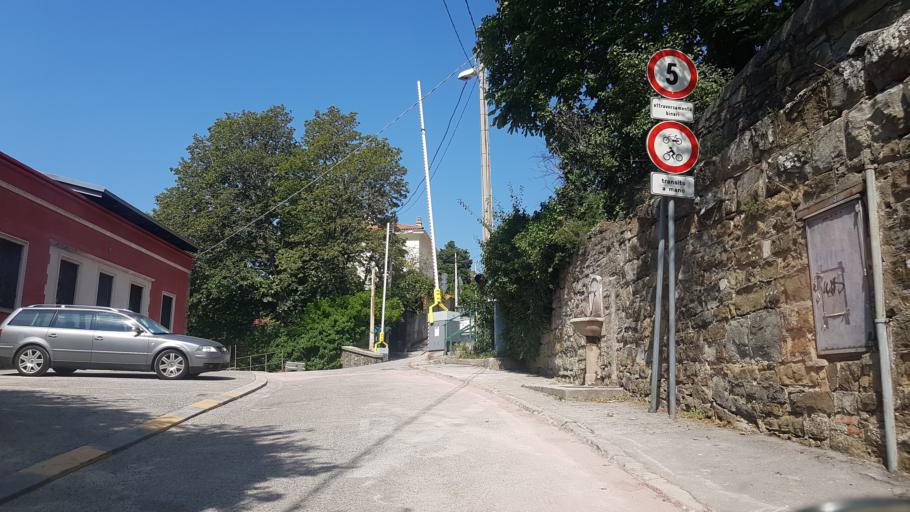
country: IT
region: Friuli Venezia Giulia
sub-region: Provincia di Trieste
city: Trieste
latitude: 45.6611
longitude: 13.7786
